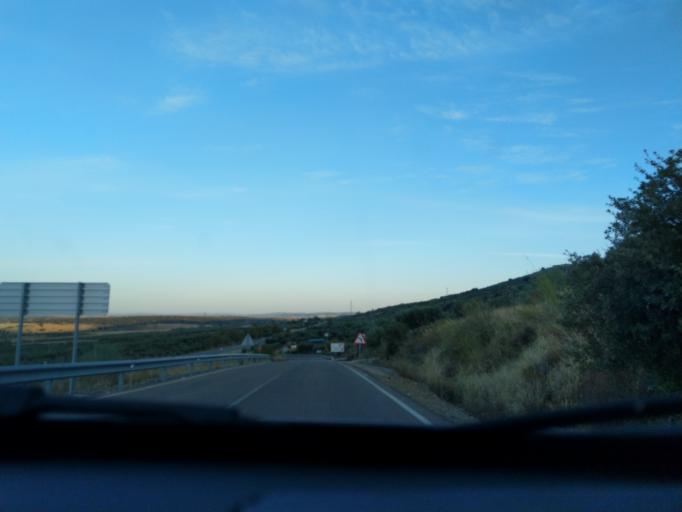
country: ES
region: Extremadura
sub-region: Provincia de Badajoz
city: Reina
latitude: 38.1893
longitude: -5.9462
